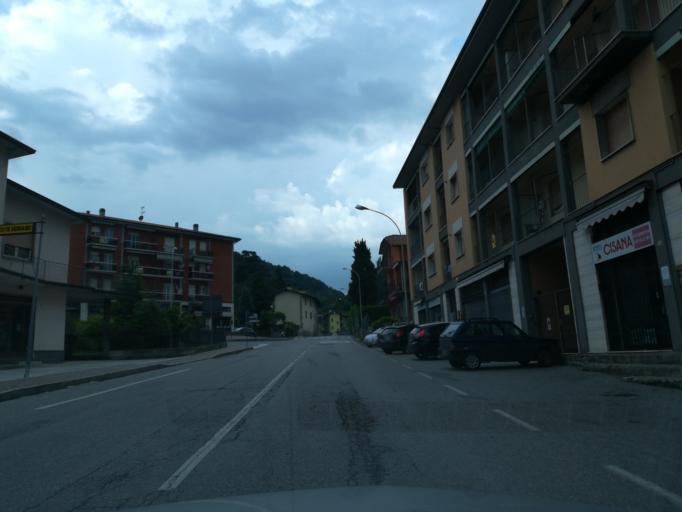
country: IT
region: Lombardy
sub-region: Provincia di Bergamo
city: Almenno San Salvatore
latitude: 45.7518
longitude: 9.5988
